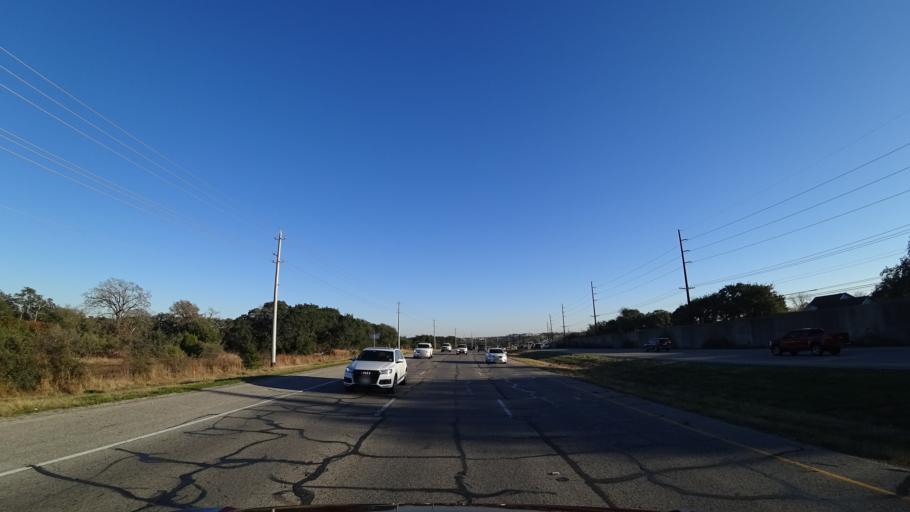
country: US
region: Texas
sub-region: Williamson County
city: Jollyville
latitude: 30.4490
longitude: -97.7457
